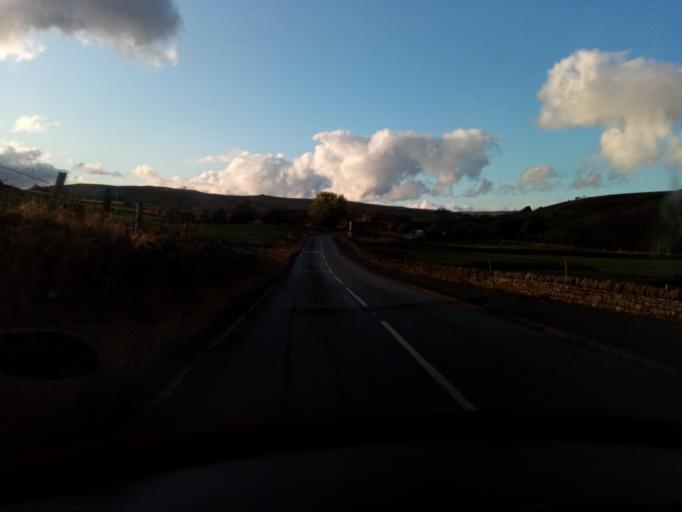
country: GB
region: England
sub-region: County Durham
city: Newbiggin
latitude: 54.7464
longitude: -2.2134
